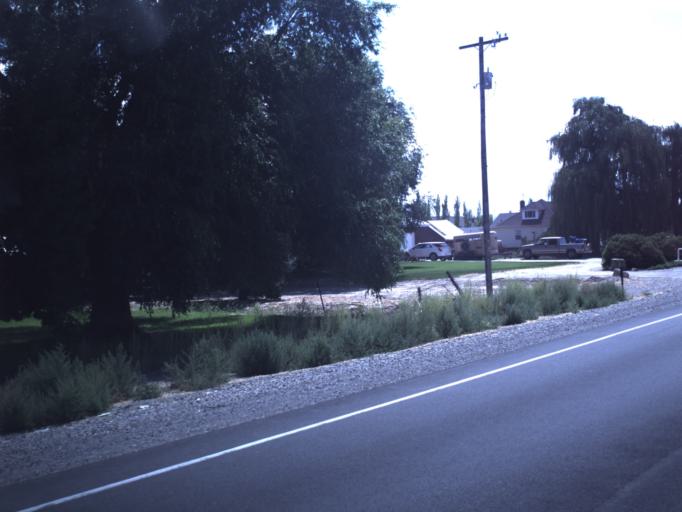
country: US
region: Utah
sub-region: Box Elder County
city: Elwood
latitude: 41.6926
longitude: -112.1416
